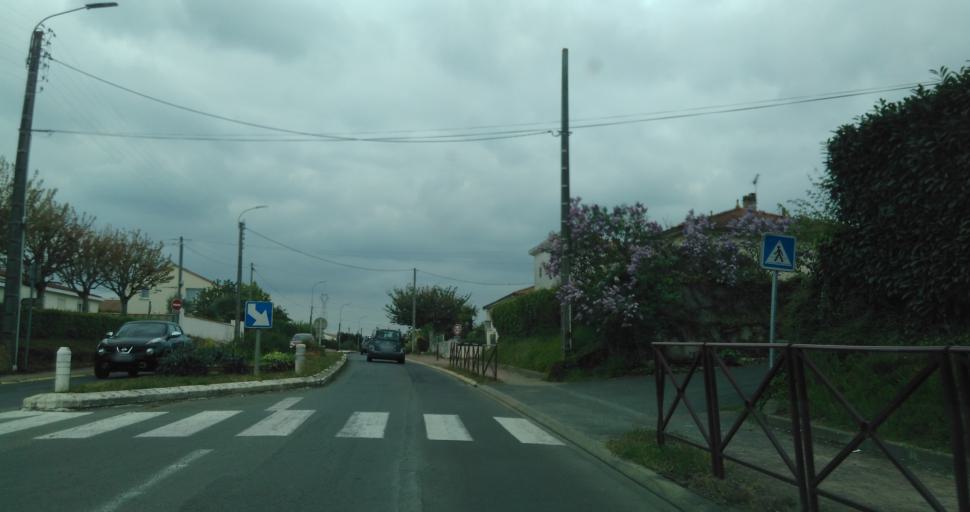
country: FR
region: Poitou-Charentes
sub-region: Departement des Deux-Sevres
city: Magne
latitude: 46.3154
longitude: -0.5483
